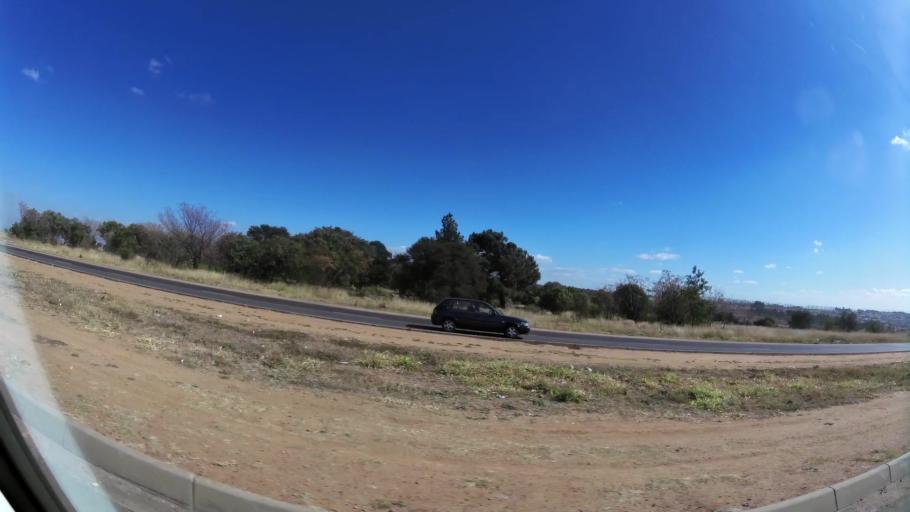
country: ZA
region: Gauteng
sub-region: City of Johannesburg Metropolitan Municipality
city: Midrand
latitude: -25.9382
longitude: 28.0958
